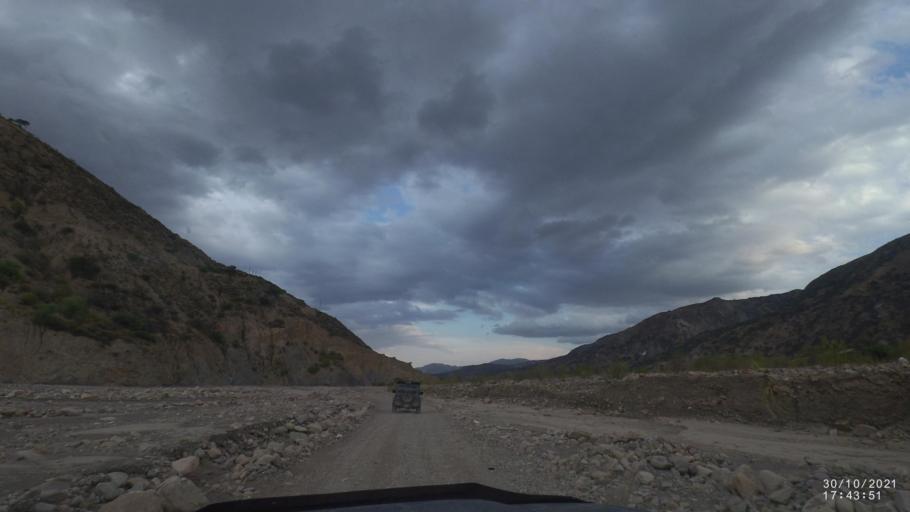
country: BO
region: Cochabamba
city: Sipe Sipe
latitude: -17.5265
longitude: -66.5367
